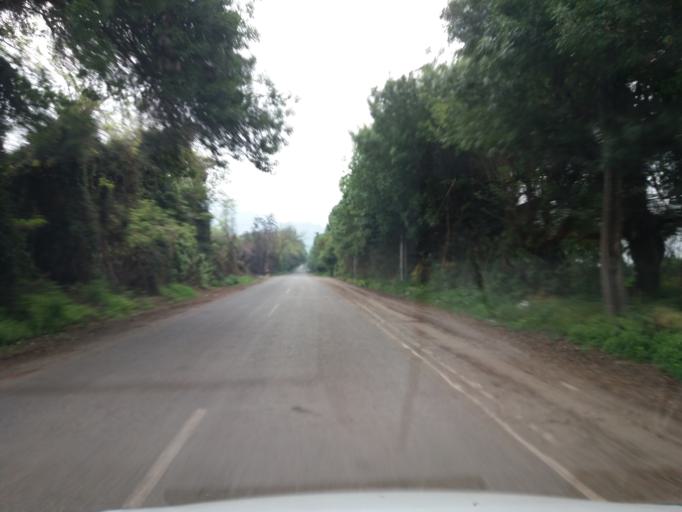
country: CL
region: Valparaiso
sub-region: Provincia de Quillota
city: Hacienda La Calera
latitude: -32.8546
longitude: -71.1040
